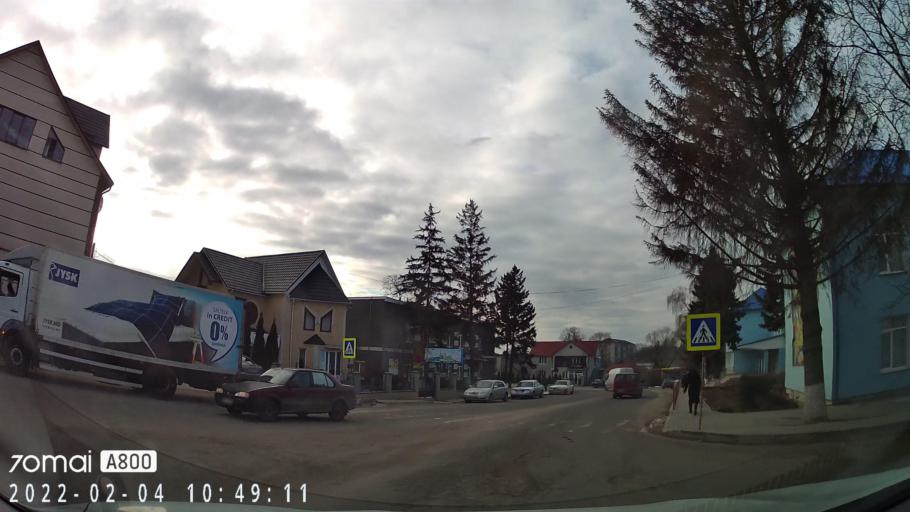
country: MD
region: Briceni
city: Briceni
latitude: 48.3591
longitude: 27.0891
